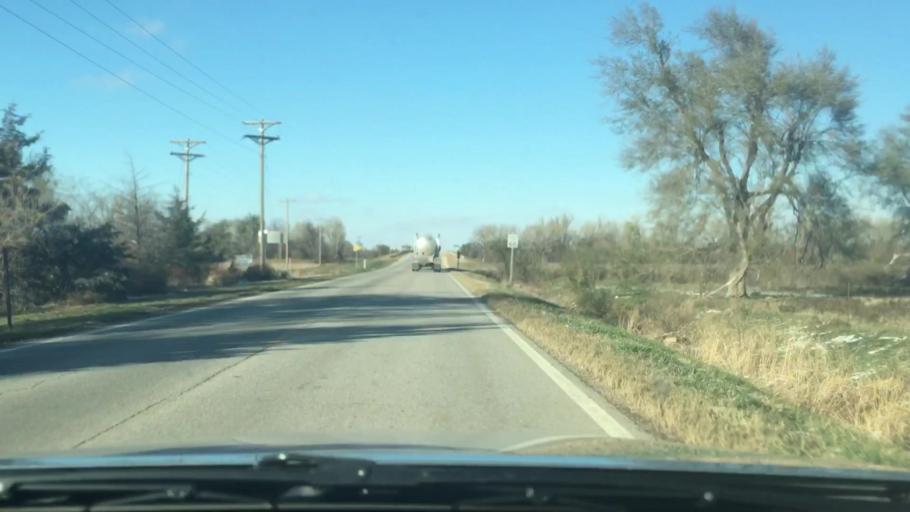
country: US
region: Kansas
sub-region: Rice County
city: Sterling
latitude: 38.1669
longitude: -98.2067
